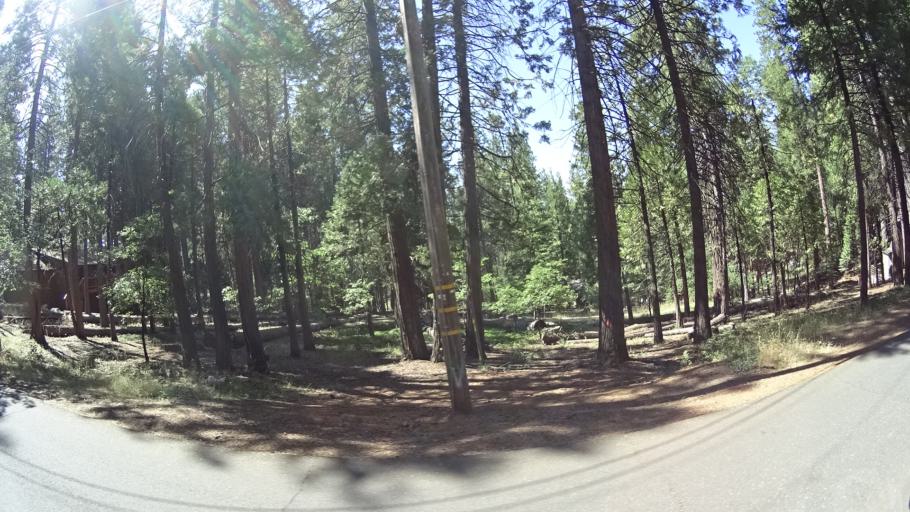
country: US
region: California
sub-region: Calaveras County
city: Arnold
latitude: 38.2432
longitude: -120.3661
